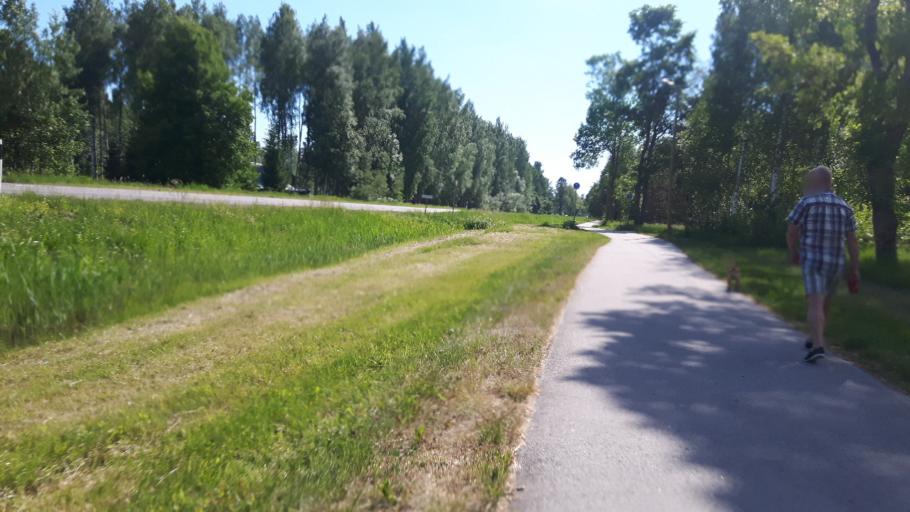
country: EE
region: Paernumaa
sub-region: Paikuse vald
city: Paikuse
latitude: 58.3849
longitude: 24.6378
